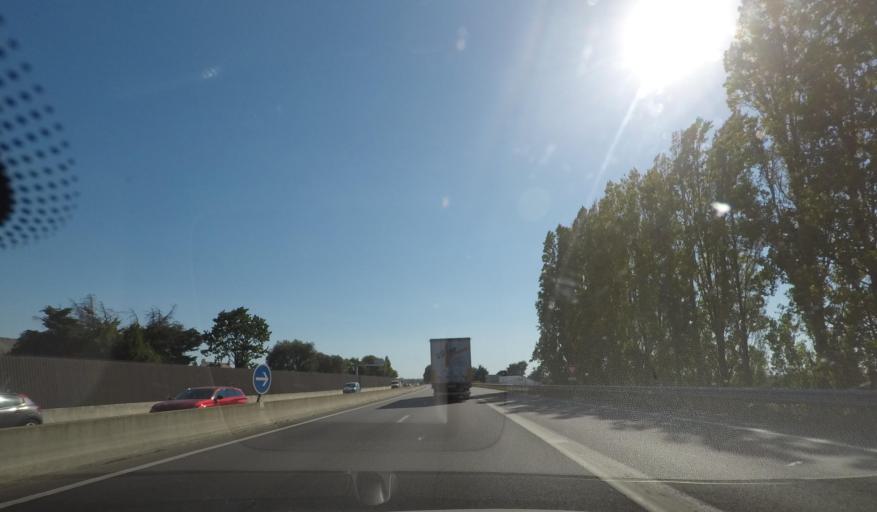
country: FR
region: Pays de la Loire
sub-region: Departement de la Loire-Atlantique
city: Trignac
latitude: 47.3184
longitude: -2.1944
